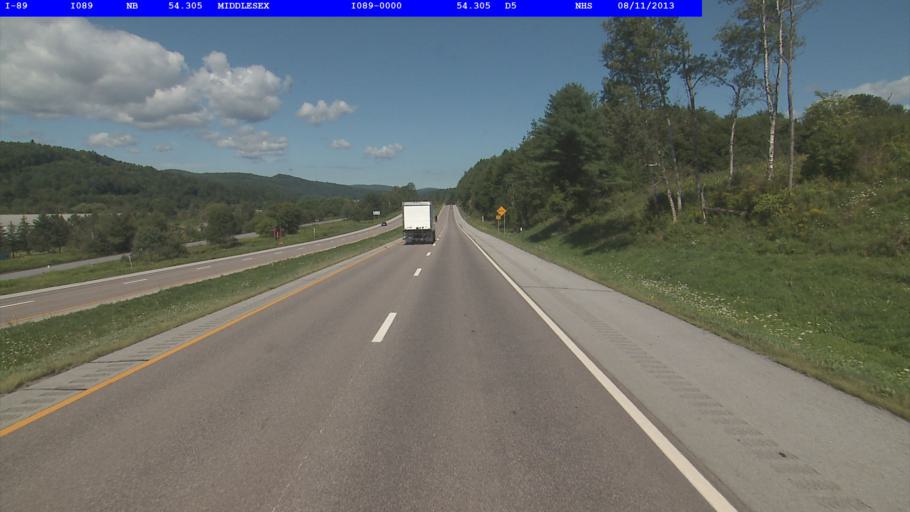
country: US
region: Vermont
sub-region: Washington County
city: Montpelier
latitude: 44.2629
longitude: -72.6147
